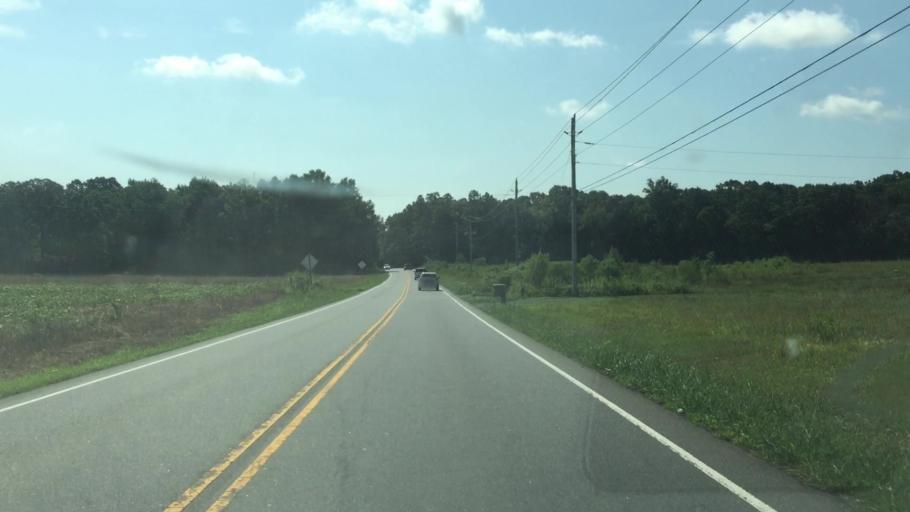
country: US
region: North Carolina
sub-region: Mecklenburg County
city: Mint Hill
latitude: 35.1674
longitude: -80.5964
